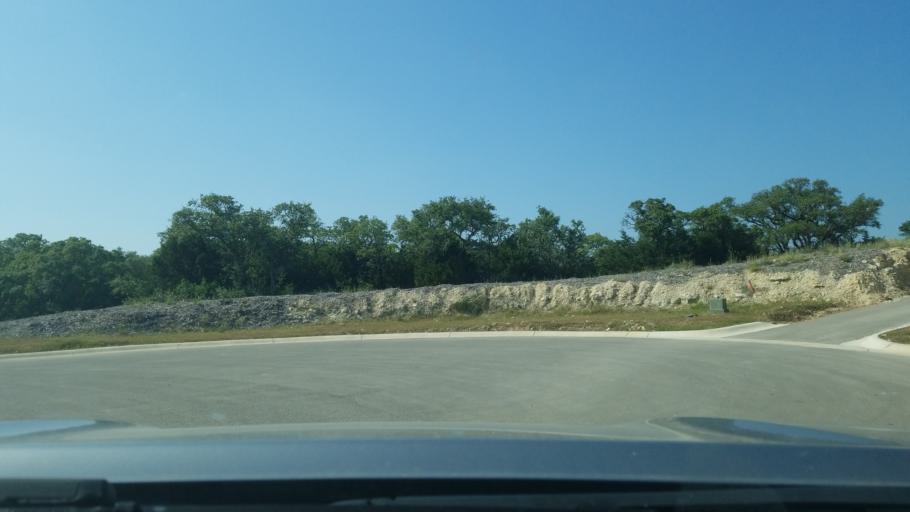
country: US
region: Texas
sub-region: Comal County
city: Bulverde
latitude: 29.7641
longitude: -98.4182
